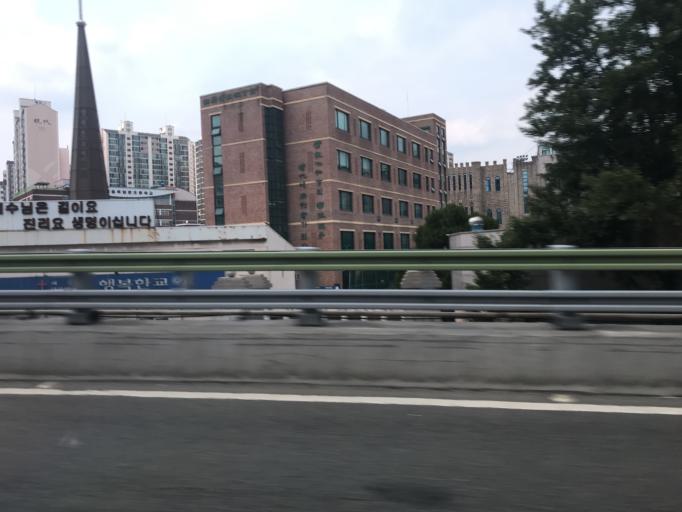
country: KR
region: Seoul
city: Seoul
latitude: 37.5725
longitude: 126.9616
